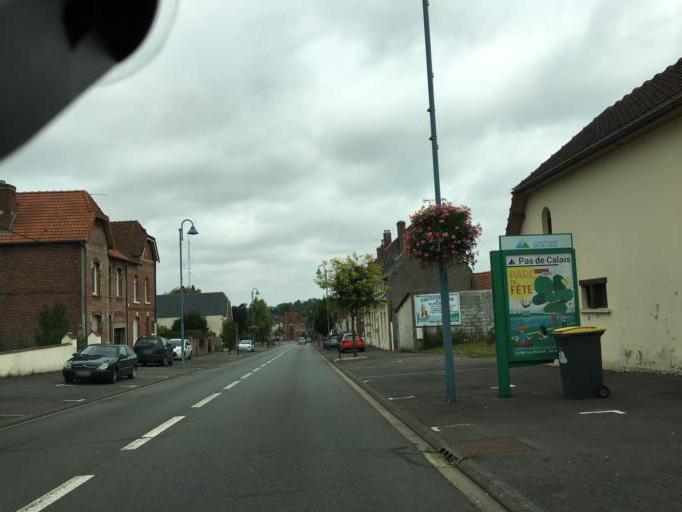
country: FR
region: Nord-Pas-de-Calais
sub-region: Departement du Pas-de-Calais
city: Saint-Pol-sur-Ternoise
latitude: 50.3748
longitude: 2.3330
